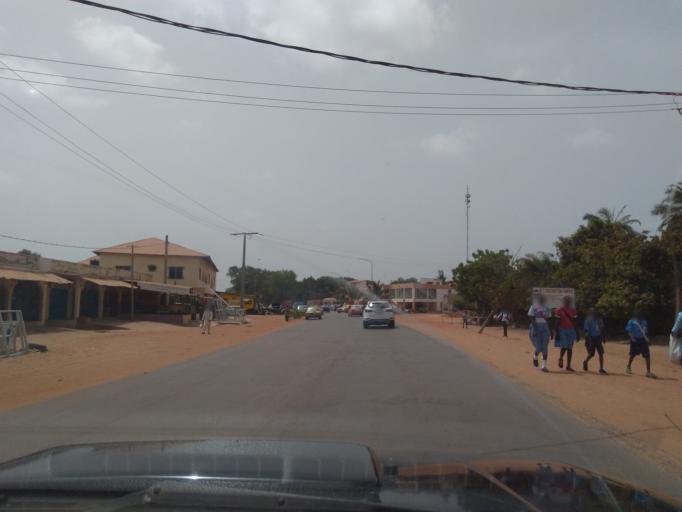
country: GM
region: Western
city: Sukuta
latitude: 13.4382
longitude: -16.7010
